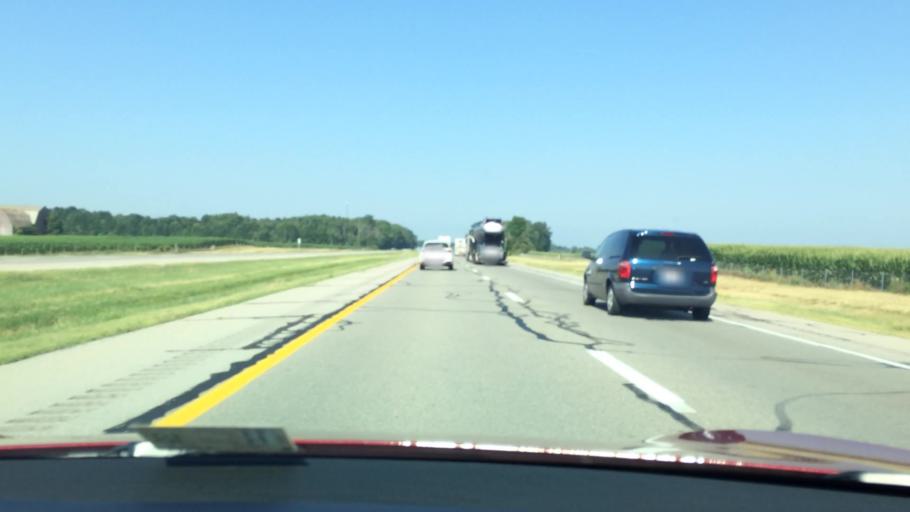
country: US
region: Ohio
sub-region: Williams County
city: Montpelier
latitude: 41.6180
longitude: -84.6130
